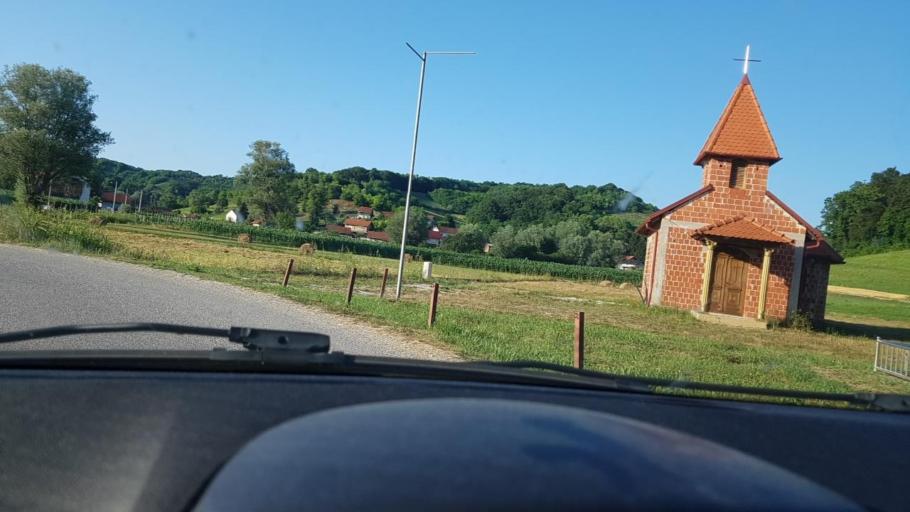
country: HR
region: Krapinsko-Zagorska
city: Zabok
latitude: 46.0848
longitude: 15.9361
